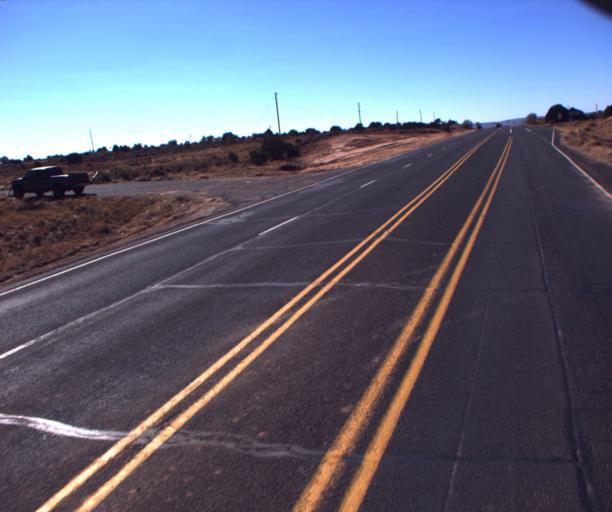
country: US
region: Arizona
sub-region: Apache County
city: Ganado
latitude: 35.7107
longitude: -109.5148
